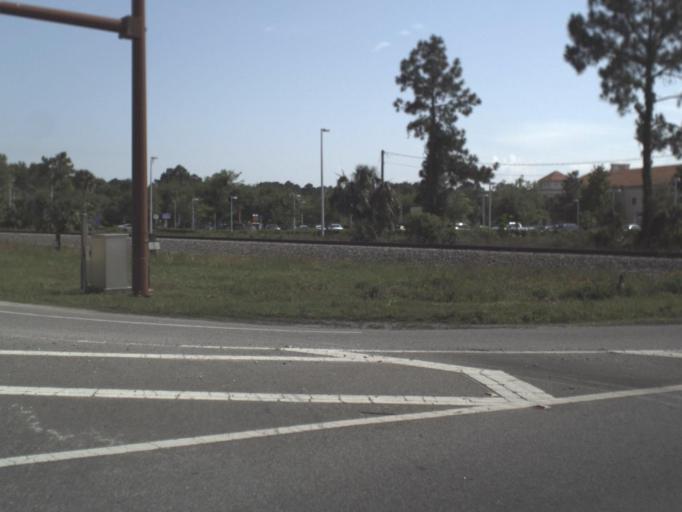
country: US
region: Florida
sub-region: Saint Johns County
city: Villano Beach
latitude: 29.9403
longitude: -81.3351
